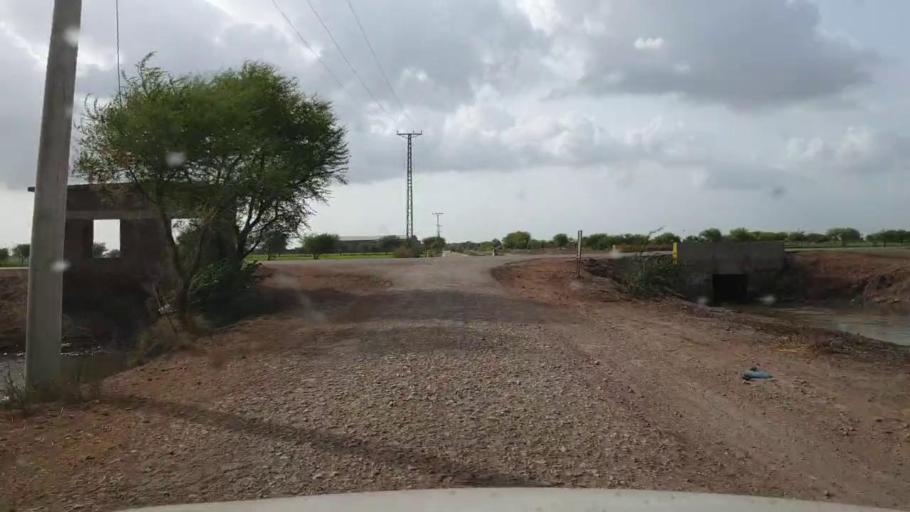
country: PK
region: Sindh
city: Kario
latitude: 24.7813
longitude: 68.5880
